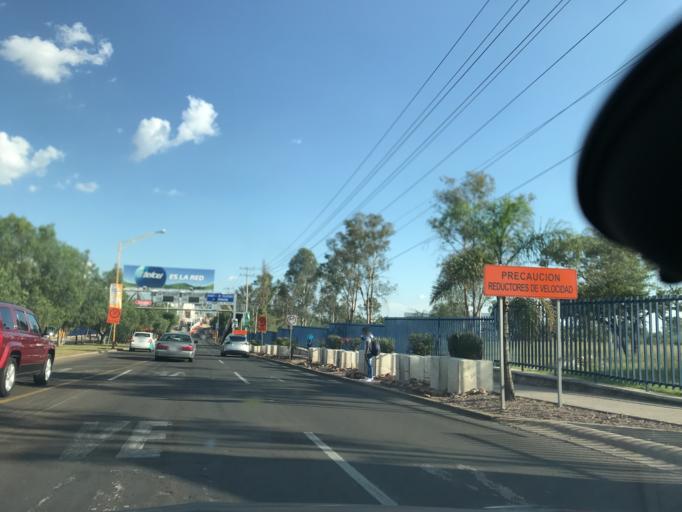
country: MX
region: Aguascalientes
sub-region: Aguascalientes
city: Pocitos
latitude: 21.9138
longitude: -102.3189
